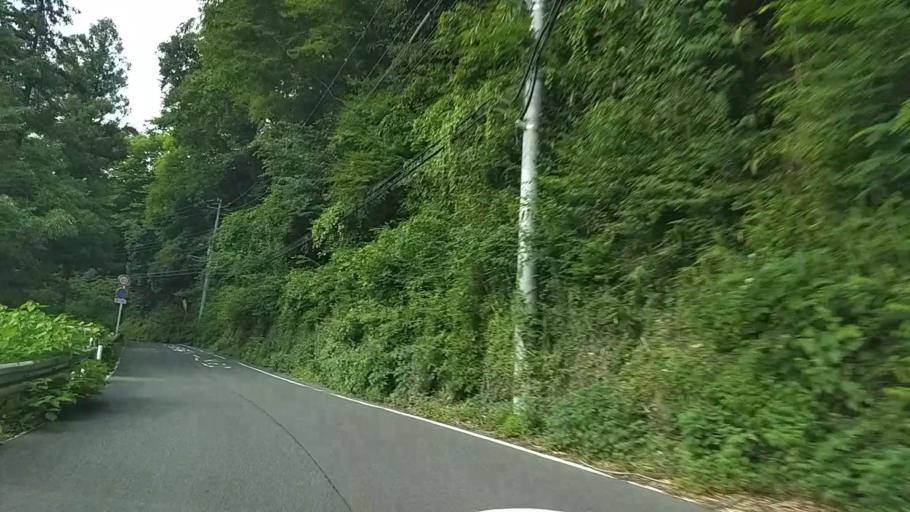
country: JP
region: Yamanashi
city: Uenohara
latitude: 35.6090
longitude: 139.1555
